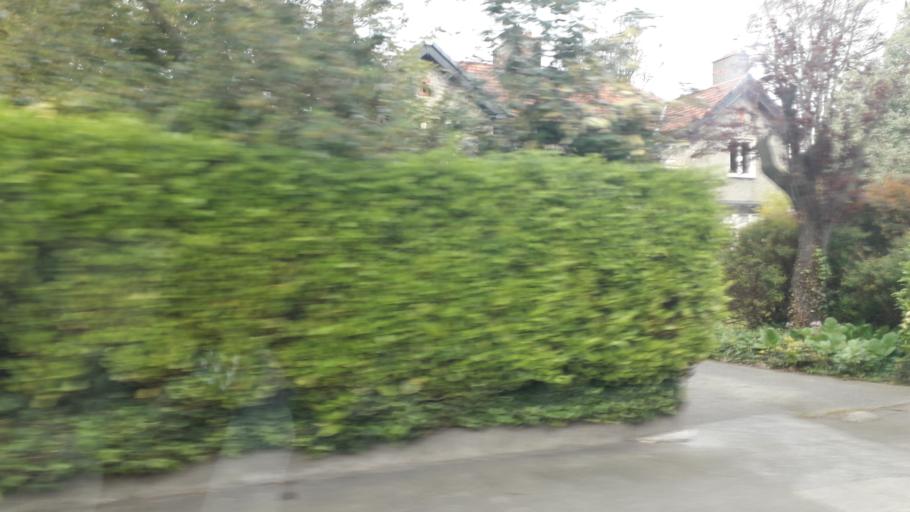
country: IE
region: Leinster
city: Dollymount
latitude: 53.3634
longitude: -6.1872
